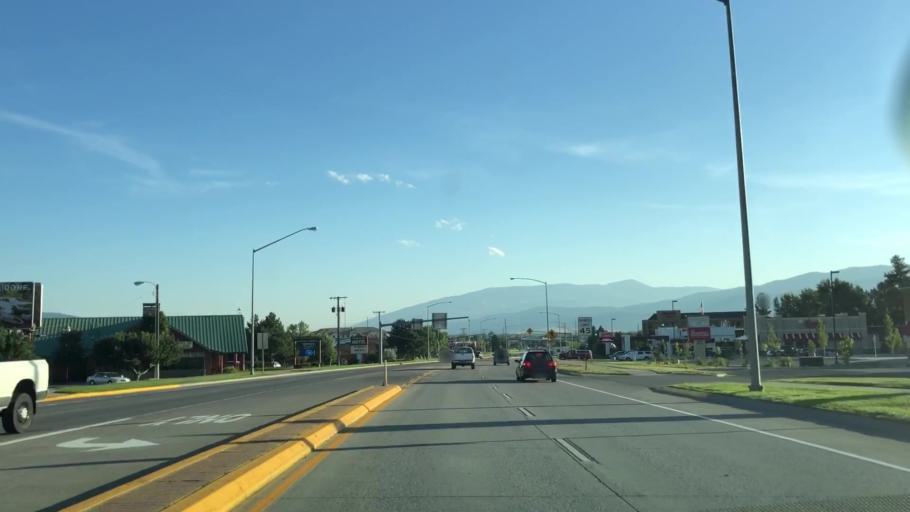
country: US
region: Montana
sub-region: Missoula County
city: Orchard Homes
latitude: 46.9110
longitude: -114.0352
